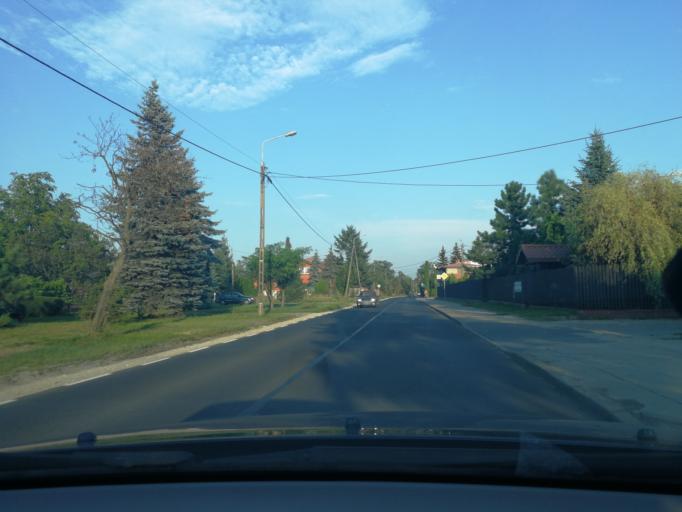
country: PL
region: Masovian Voivodeship
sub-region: Powiat warszawski zachodni
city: Ozarow Mazowiecki
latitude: 52.1890
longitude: 20.7588
